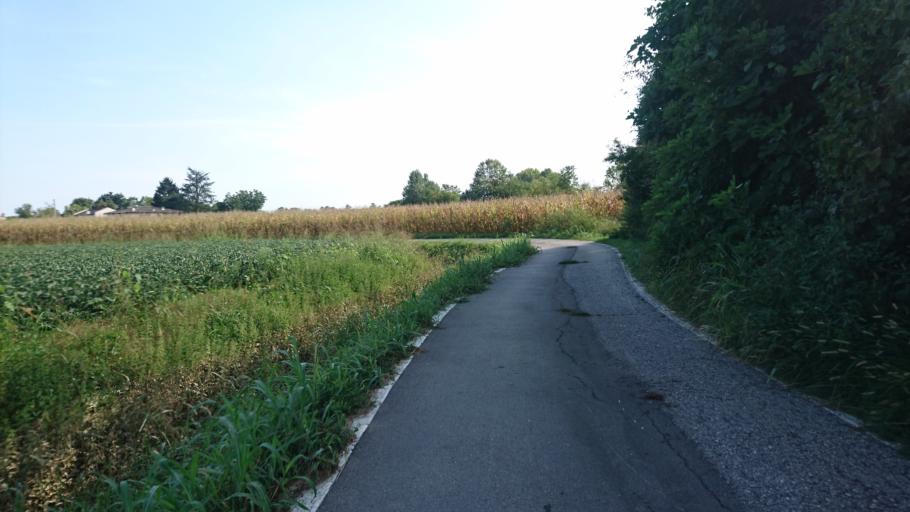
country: IT
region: Veneto
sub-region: Provincia di Padova
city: Saccolongo
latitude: 45.4068
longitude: 11.7559
